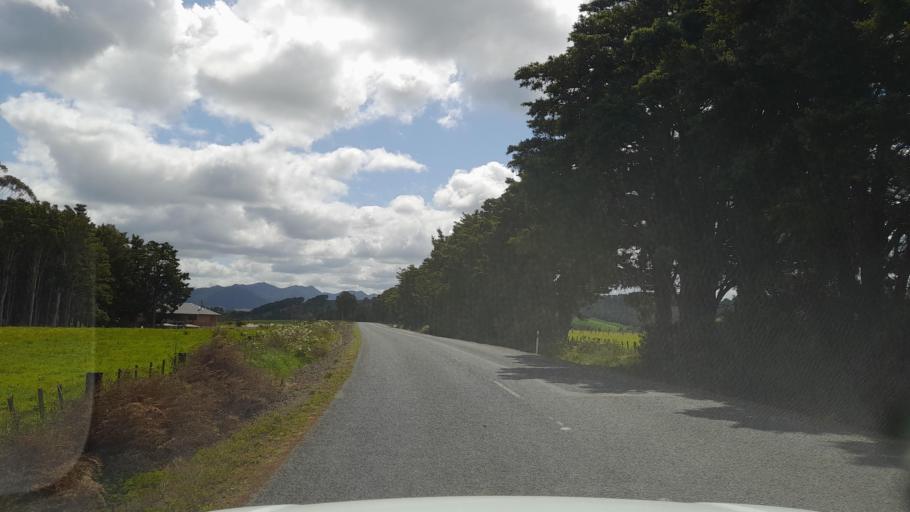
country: NZ
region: Northland
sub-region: Whangarei
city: Maungatapere
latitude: -35.7160
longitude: 174.0677
